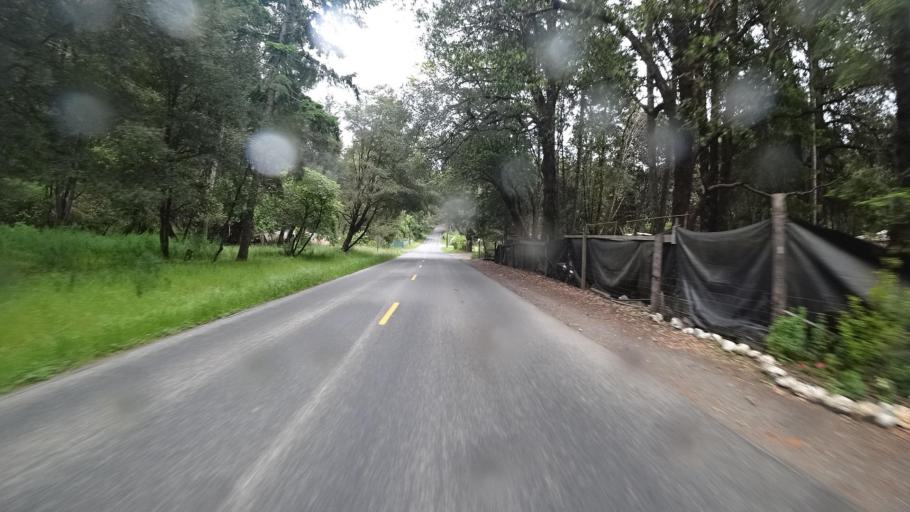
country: US
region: California
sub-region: Humboldt County
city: Willow Creek
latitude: 41.0571
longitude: -123.6732
